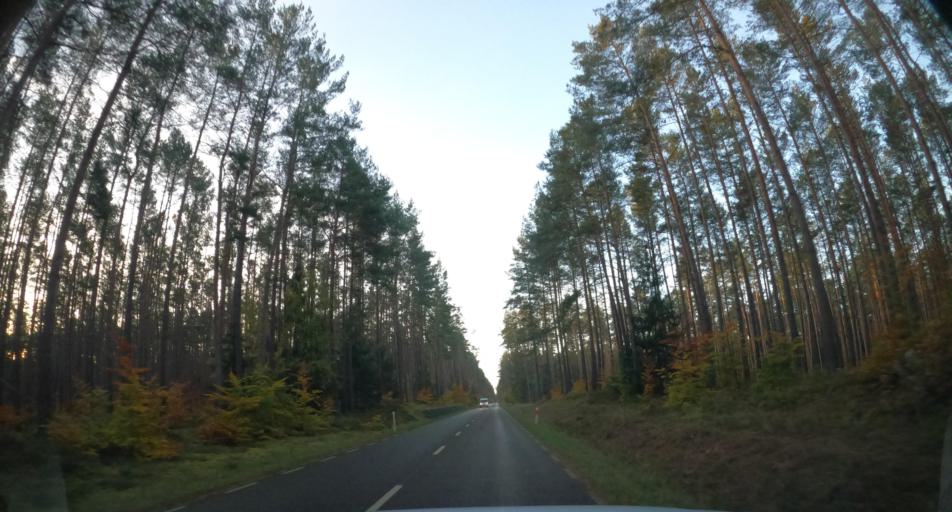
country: PL
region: West Pomeranian Voivodeship
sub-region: Powiat policki
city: Nowe Warpno
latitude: 53.6355
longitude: 14.3190
